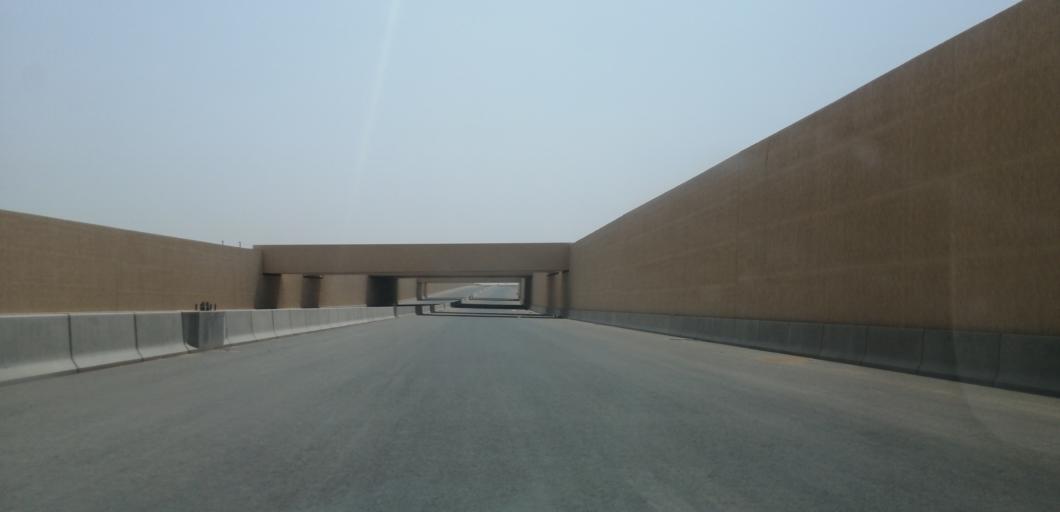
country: KW
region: Muhafazat al Jahra'
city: Al Jahra'
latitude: 29.4512
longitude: 47.6035
